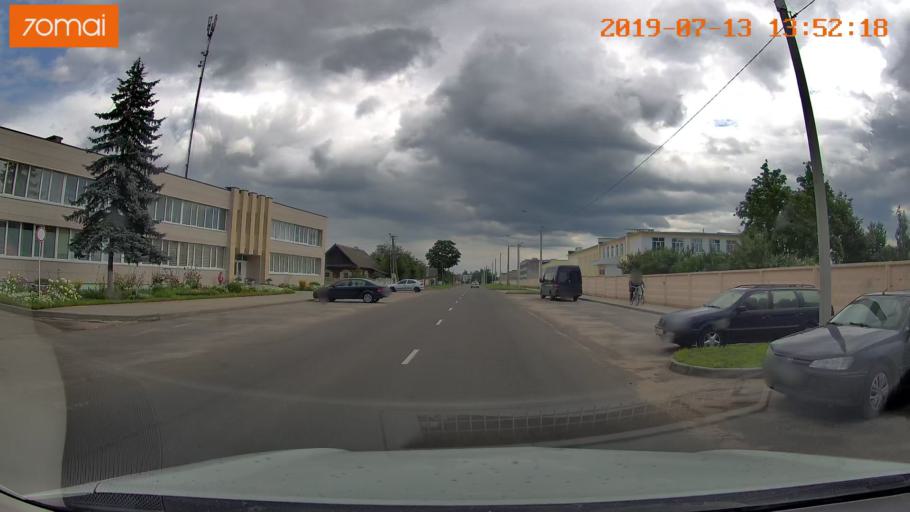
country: BY
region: Mogilev
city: Asipovichy
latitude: 53.2944
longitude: 28.6401
